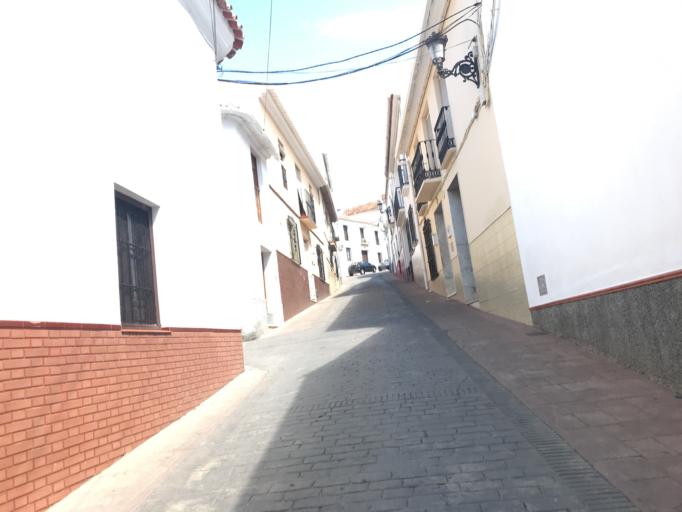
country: ES
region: Andalusia
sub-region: Provincia de Malaga
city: Periana
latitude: 36.9279
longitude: -4.1921
